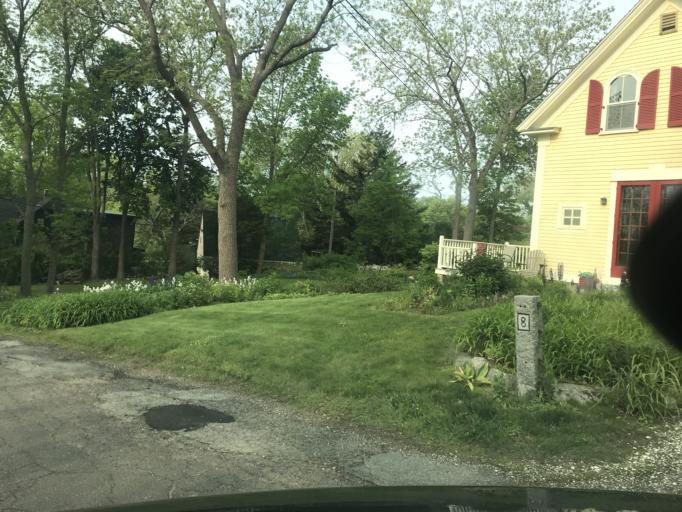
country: US
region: Massachusetts
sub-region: Essex County
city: Rockport
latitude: 42.6710
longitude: -70.6248
